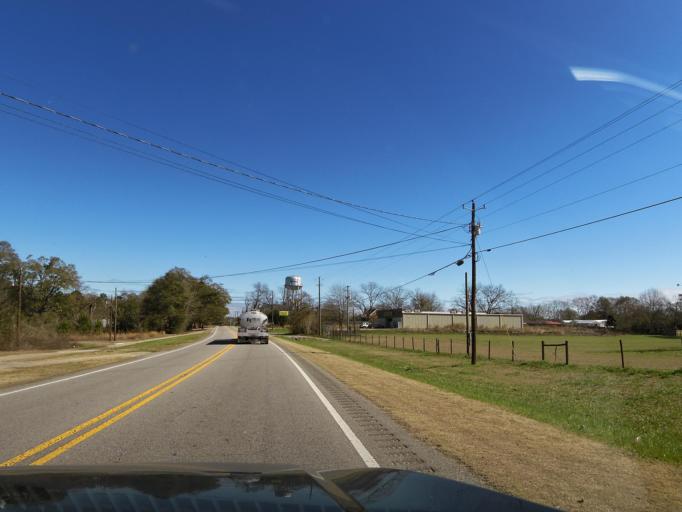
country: US
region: Alabama
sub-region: Bullock County
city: Union Springs
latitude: 32.0787
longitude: -85.5257
